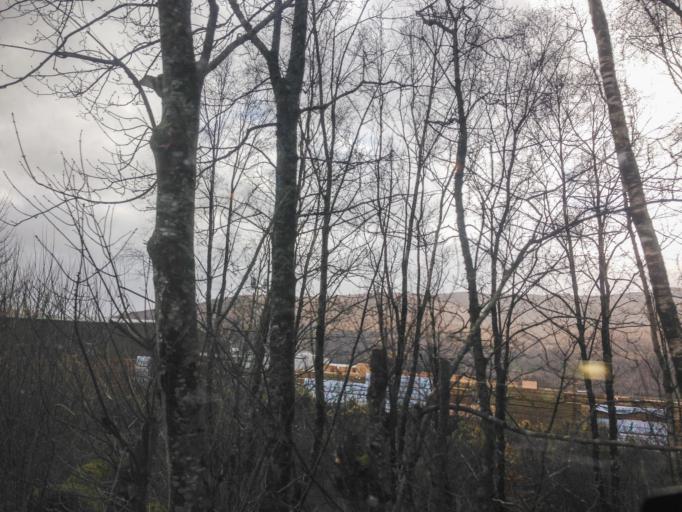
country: GB
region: Scotland
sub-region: Highland
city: Fort William
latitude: 56.8430
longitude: -5.1490
